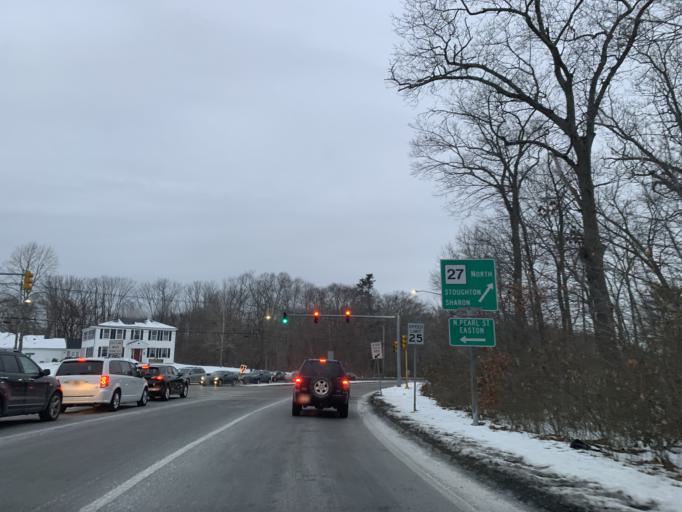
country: US
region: Massachusetts
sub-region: Norfolk County
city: Avon
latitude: 42.0964
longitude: -71.0648
